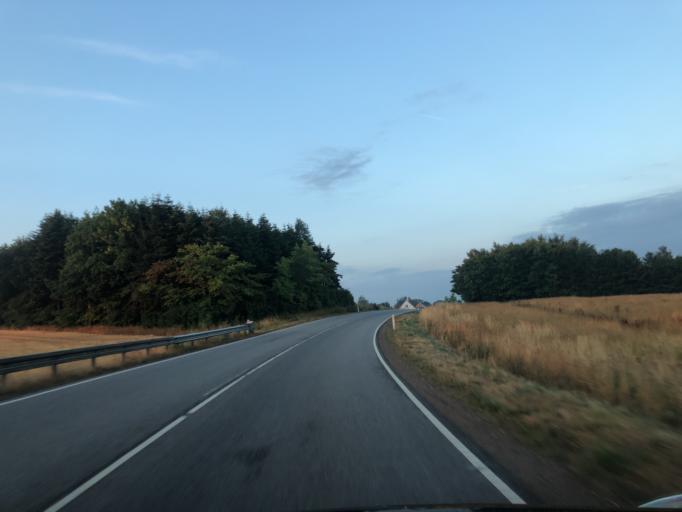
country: DK
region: Zealand
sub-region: Soro Kommune
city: Stenlille
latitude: 55.5959
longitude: 11.6594
